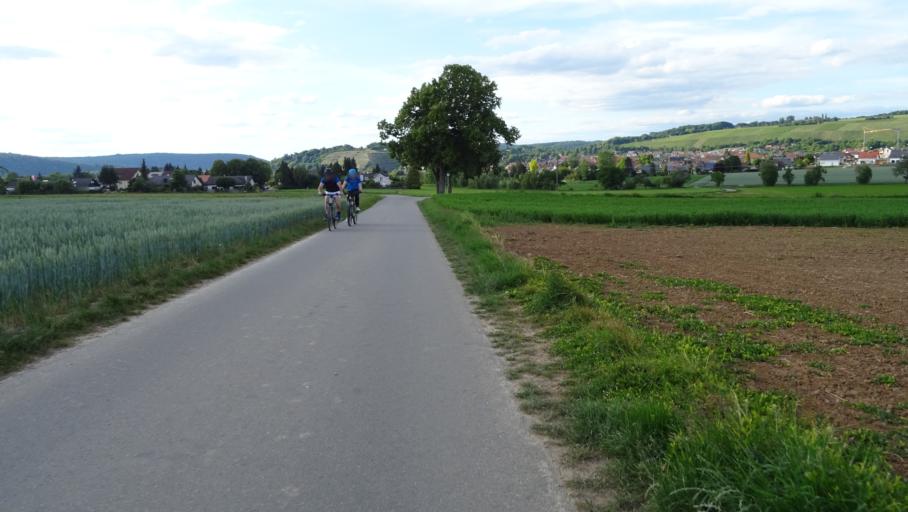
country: DE
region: Baden-Wuerttemberg
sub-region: Regierungsbezirk Stuttgart
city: Gundelsheim
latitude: 49.2722
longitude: 9.1645
